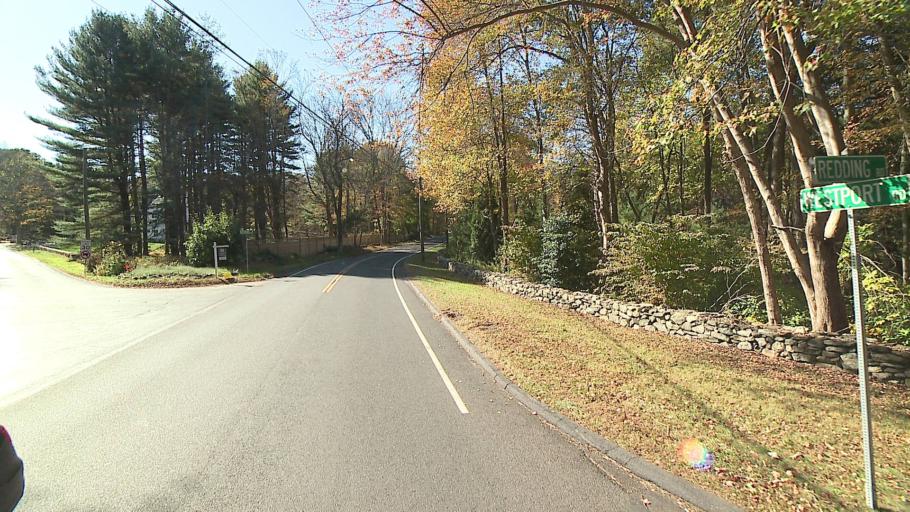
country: US
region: Connecticut
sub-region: Fairfield County
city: Westport
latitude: 41.2220
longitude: -73.3228
